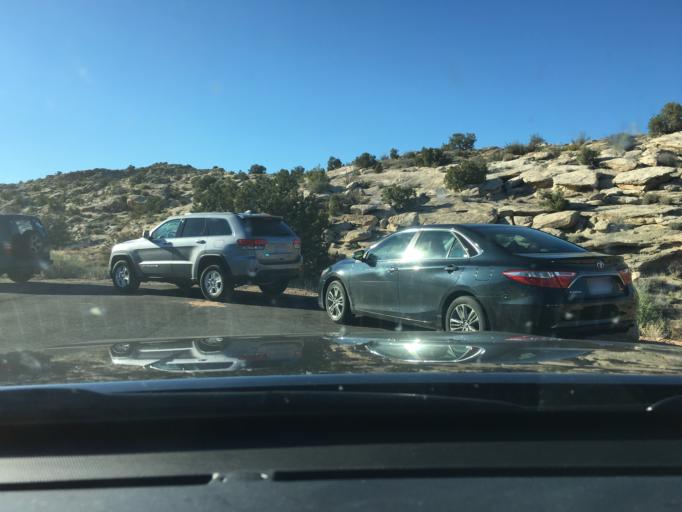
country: US
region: Utah
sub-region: Grand County
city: Moab
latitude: 38.7364
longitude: -109.5214
